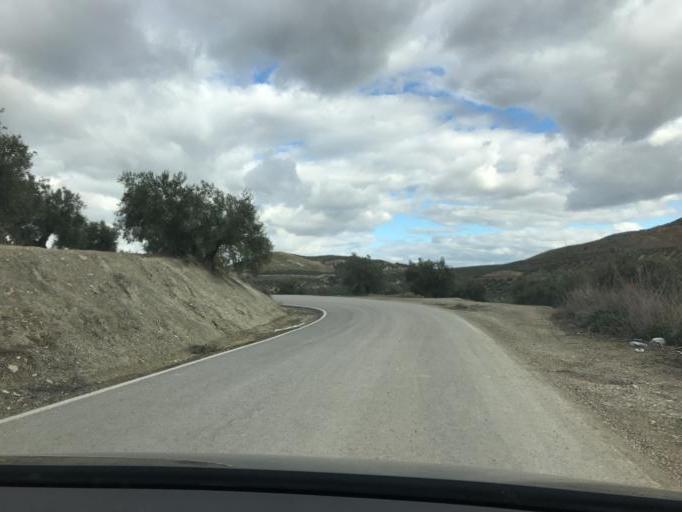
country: ES
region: Andalusia
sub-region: Provincia de Jaen
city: Jimena
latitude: 37.8850
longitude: -3.4680
